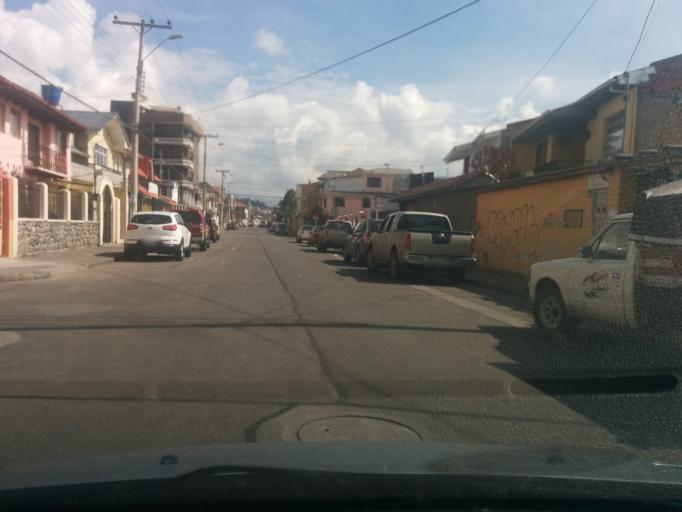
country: EC
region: Azuay
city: Cuenca
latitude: -2.9015
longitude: -78.9928
